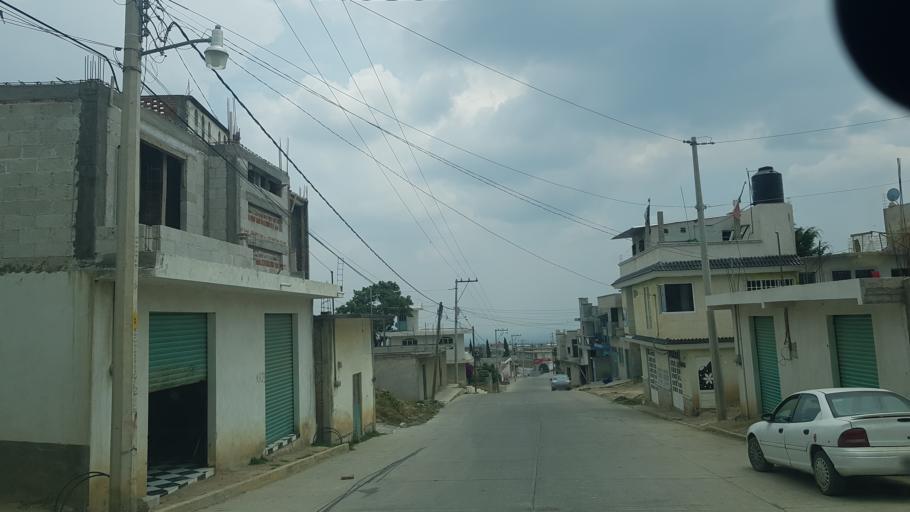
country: MX
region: Puebla
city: Domingo Arenas
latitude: 19.1520
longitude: -98.4998
